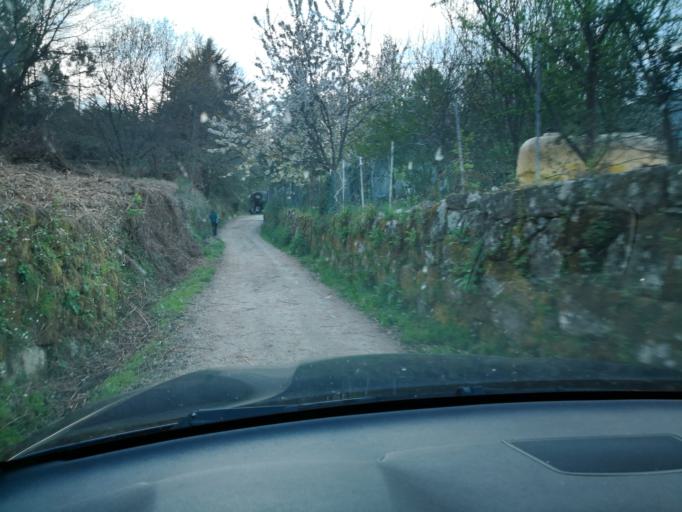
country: PT
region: Vila Real
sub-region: Vila Real
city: Vila Real
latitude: 41.3028
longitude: -7.7728
